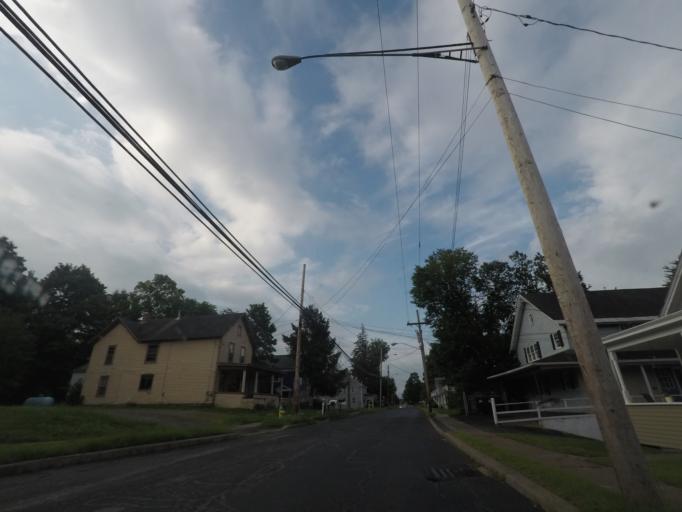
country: US
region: New York
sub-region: Rensselaer County
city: Nassau
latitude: 42.5205
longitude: -73.6081
